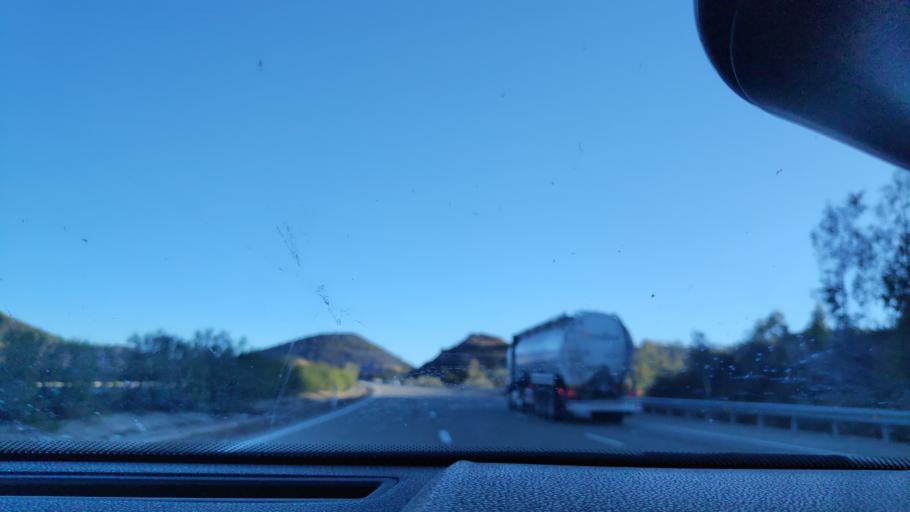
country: ES
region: Andalusia
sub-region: Provincia de Sevilla
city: El Ronquillo
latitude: 37.6646
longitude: -6.1689
